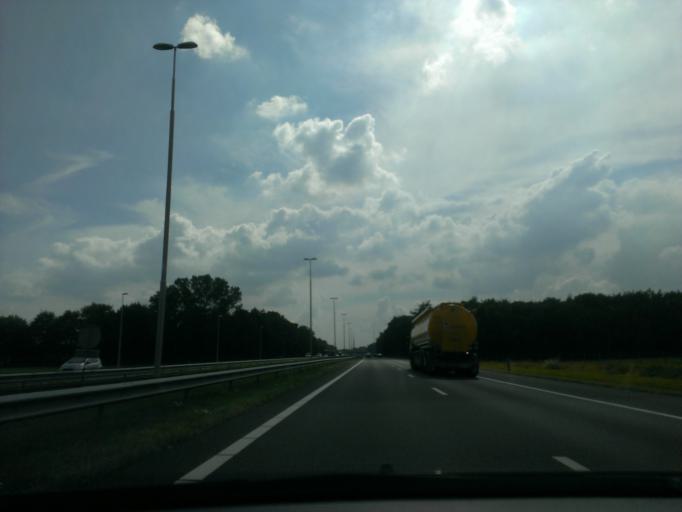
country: NL
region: Gelderland
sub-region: Gemeente Epe
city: Epe
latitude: 52.3423
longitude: 6.0135
